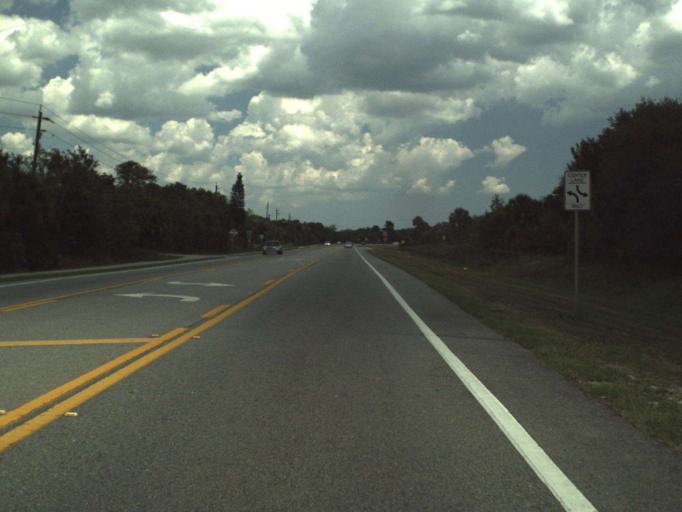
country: US
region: Florida
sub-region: Brevard County
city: Titusville
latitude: 28.5868
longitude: -80.8469
